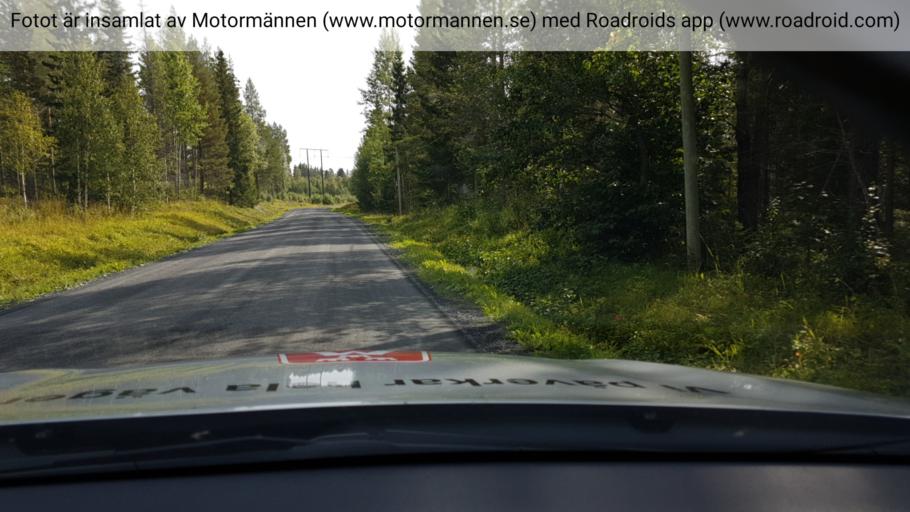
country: SE
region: Jaemtland
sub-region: Krokoms Kommun
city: Valla
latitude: 63.3420
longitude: 14.0091
